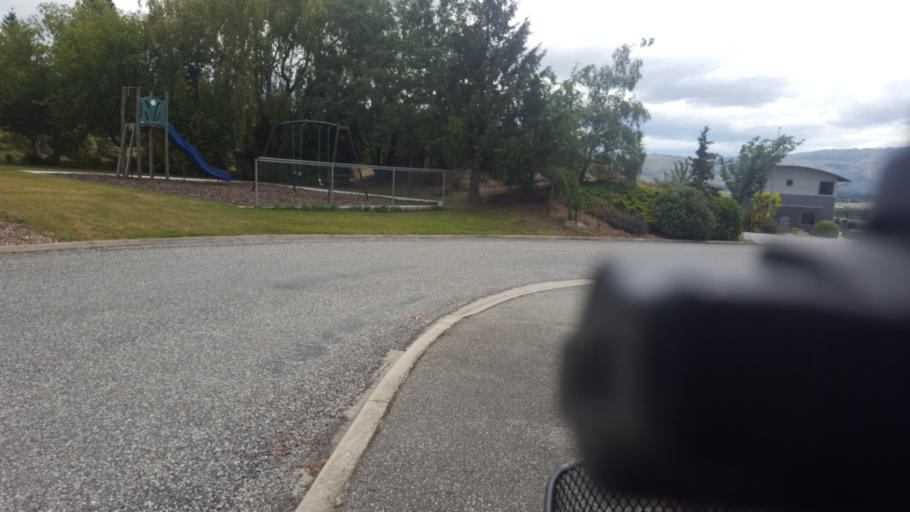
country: NZ
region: Otago
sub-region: Queenstown-Lakes District
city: Wanaka
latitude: -45.2596
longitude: 169.3803
